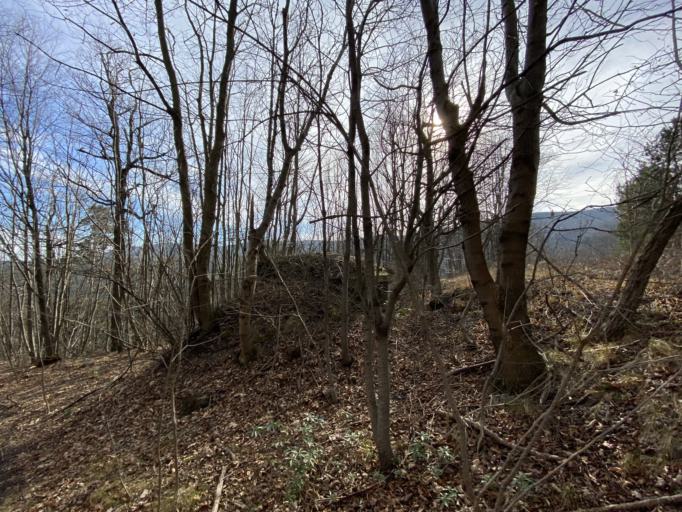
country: AT
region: Lower Austria
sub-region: Politischer Bezirk Baden
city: Heiligenkreuz
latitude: 48.0099
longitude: 16.1562
